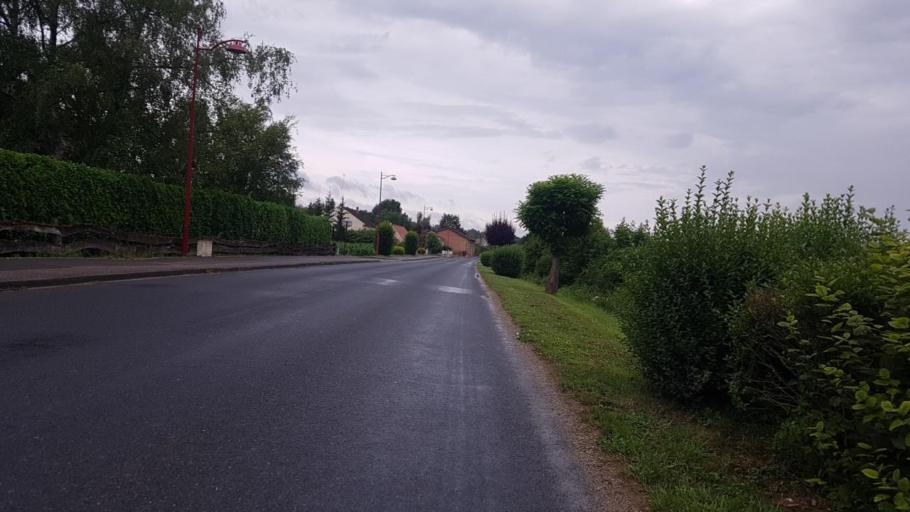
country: FR
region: Champagne-Ardenne
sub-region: Departement de la Marne
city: Vitry-le-Francois
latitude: 48.7420
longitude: 4.6336
